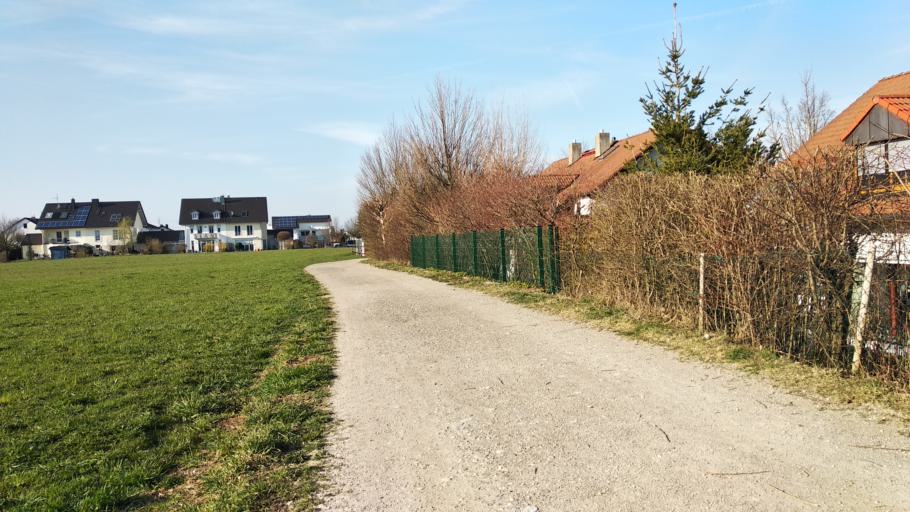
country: DE
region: Bavaria
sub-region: Upper Bavaria
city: Markt Schwaben
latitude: 48.1856
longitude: 11.8636
